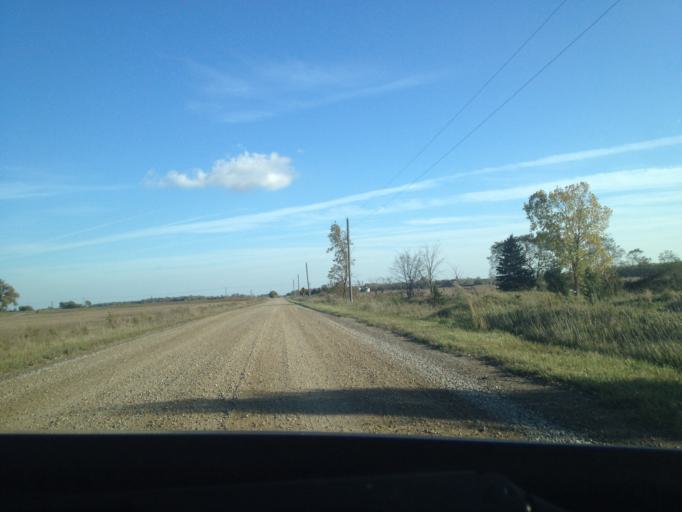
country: CA
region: Ontario
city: Delaware
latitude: 42.6514
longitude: -81.5471
